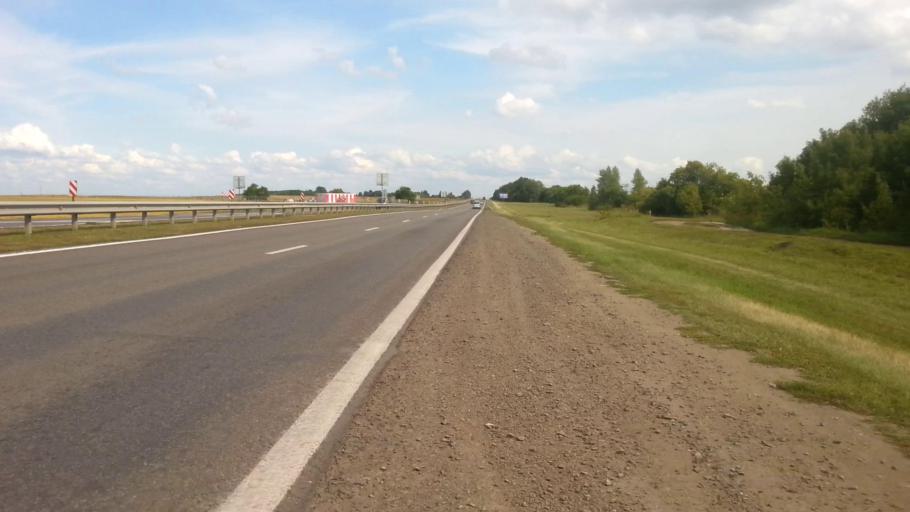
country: RU
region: Altai Krai
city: Nauchnyy Gorodok
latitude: 53.3565
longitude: 83.5091
